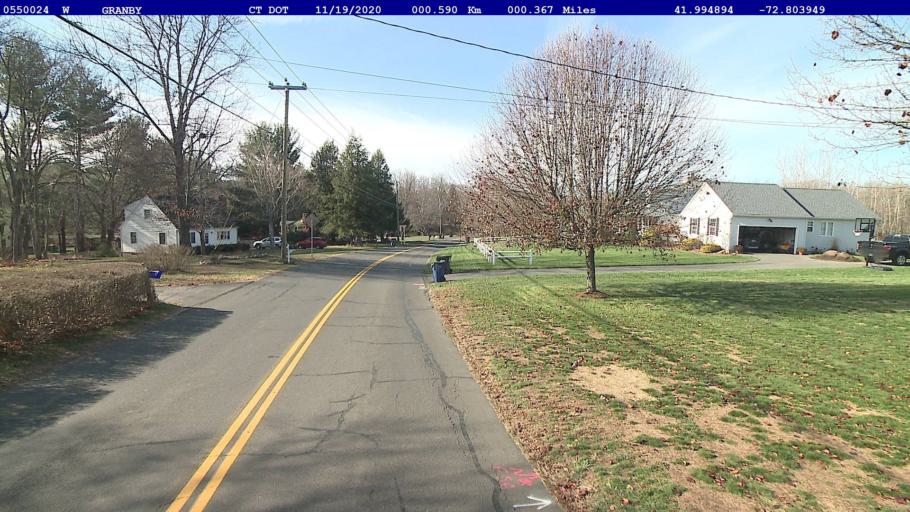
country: US
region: Connecticut
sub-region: Hartford County
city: North Granby
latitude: 41.9949
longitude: -72.8040
